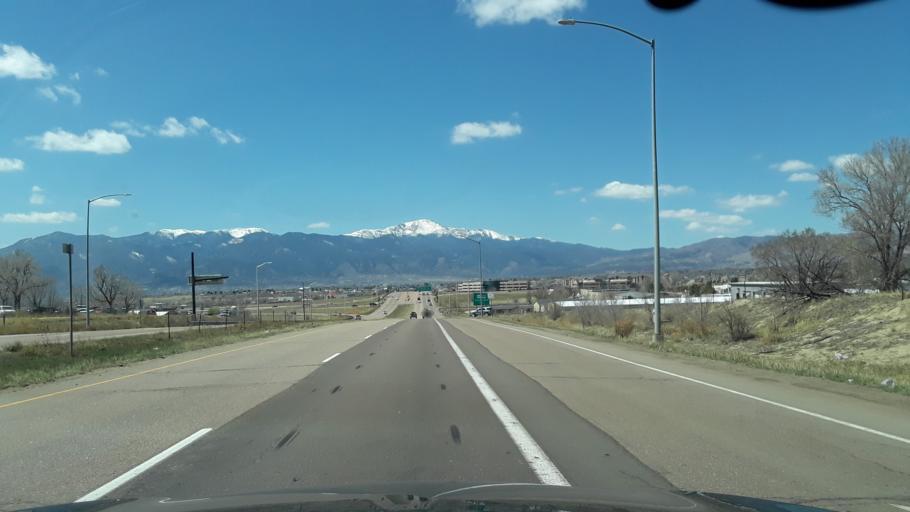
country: US
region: Colorado
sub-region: El Paso County
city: Cimarron Hills
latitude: 38.8392
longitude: -104.7123
